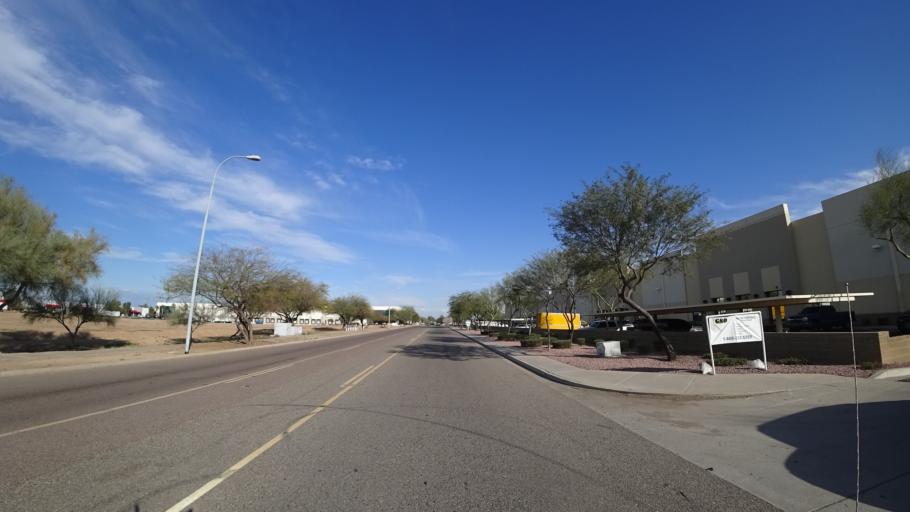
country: US
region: Arizona
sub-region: Maricopa County
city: Tolleson
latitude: 33.4587
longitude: -112.2160
